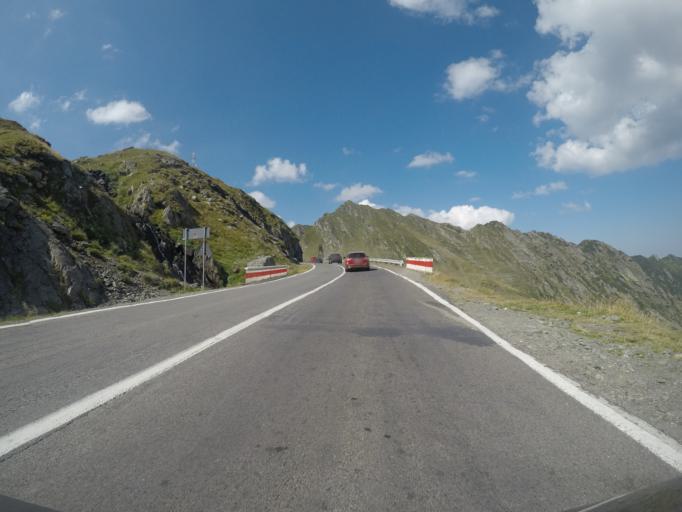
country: RO
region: Sibiu
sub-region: Comuna Cartisoara
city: Cartisoara
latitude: 45.6059
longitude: 24.6205
